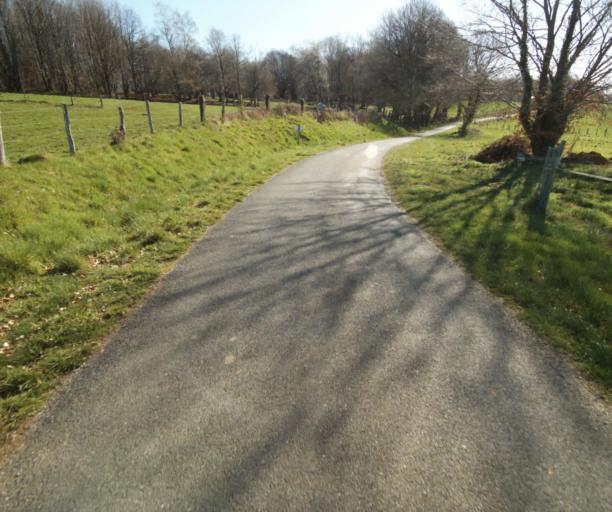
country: FR
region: Limousin
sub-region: Departement de la Correze
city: Seilhac
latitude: 45.3933
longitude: 1.7489
